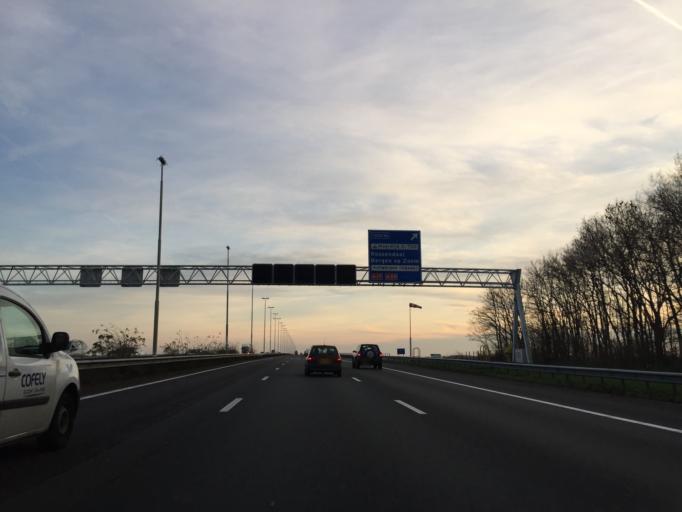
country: NL
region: South Holland
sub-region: Gemeente Strijen
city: Strijen
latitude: 51.7224
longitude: 4.6336
